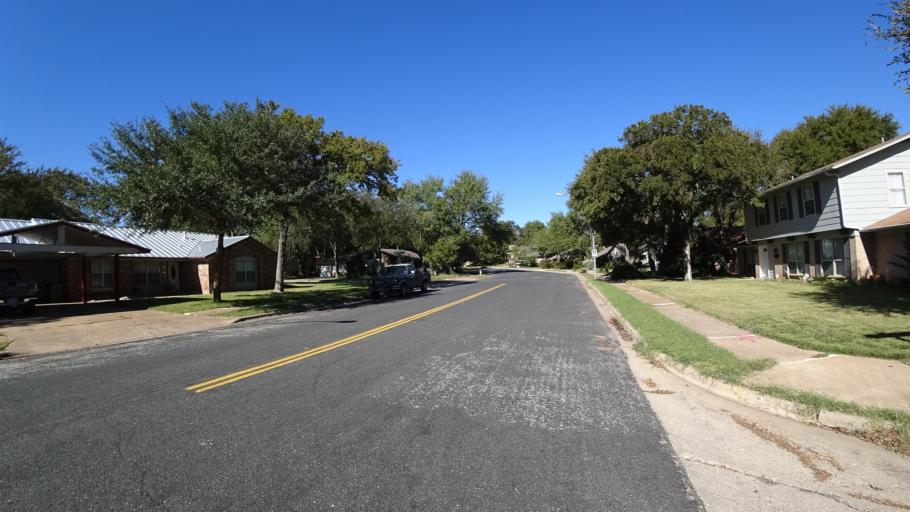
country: US
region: Texas
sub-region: Travis County
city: Rollingwood
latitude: 30.2196
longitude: -97.8079
